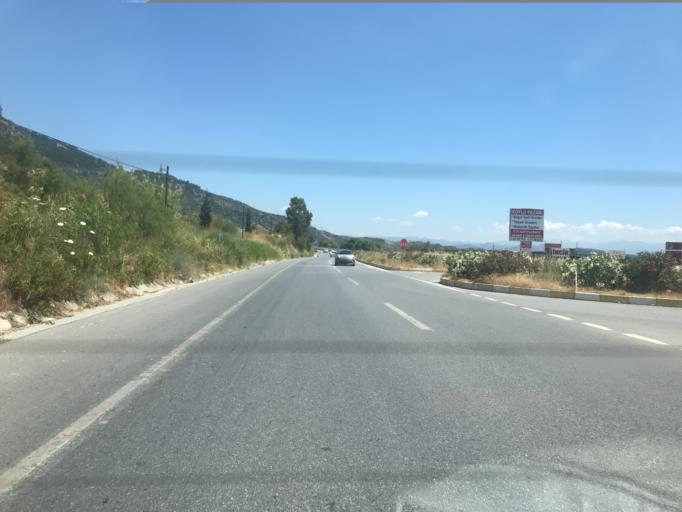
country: TR
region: Aydin
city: Ortaklar
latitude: 37.8138
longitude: 27.4845
